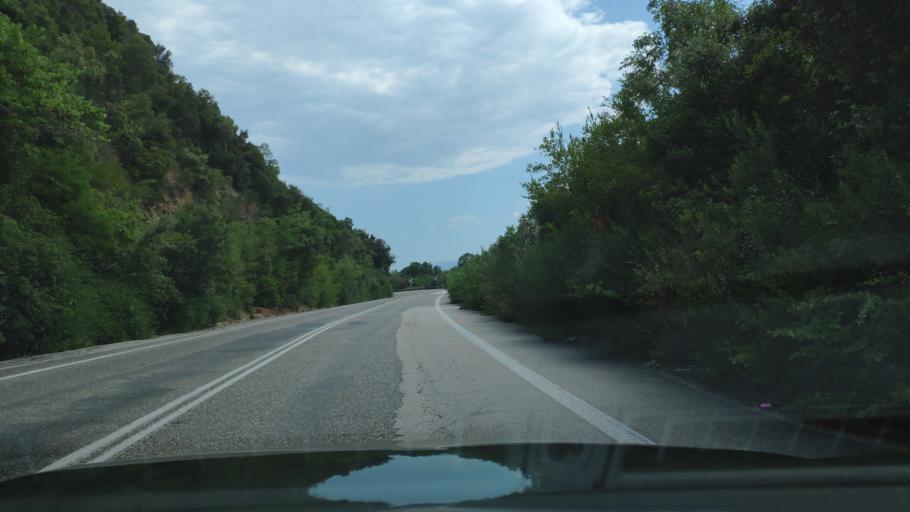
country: GR
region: West Greece
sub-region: Nomos Aitolias kai Akarnanias
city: Menidi
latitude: 39.0044
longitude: 21.1476
